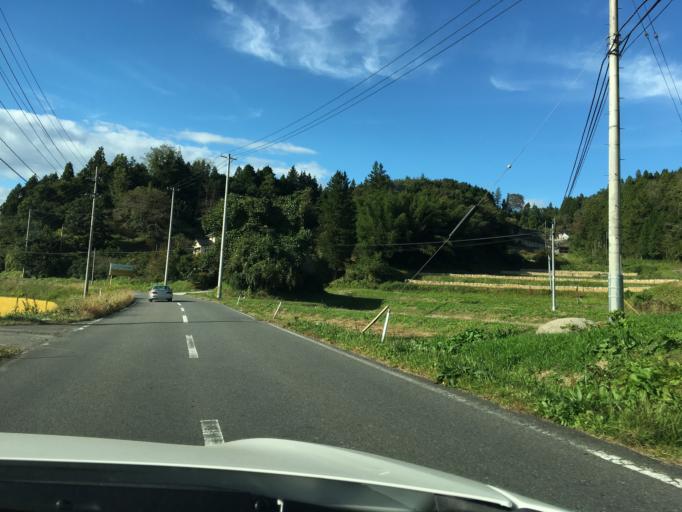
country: JP
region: Fukushima
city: Ishikawa
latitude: 37.1826
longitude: 140.4625
